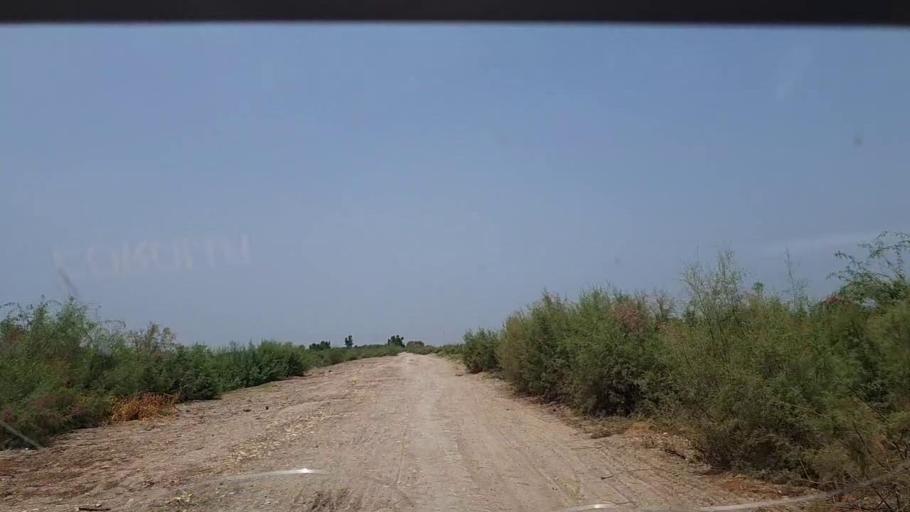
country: PK
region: Sindh
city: Adilpur
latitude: 27.9000
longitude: 69.2335
